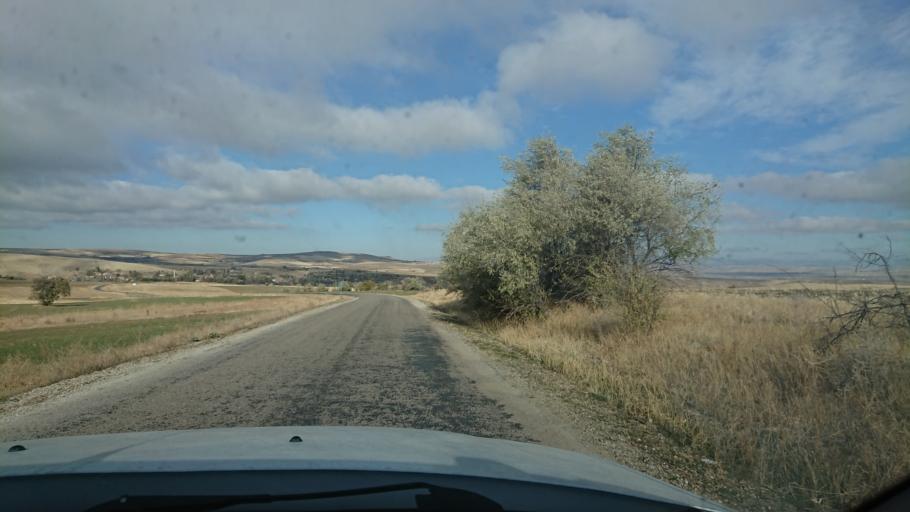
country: TR
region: Aksaray
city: Ortakoy
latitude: 38.7966
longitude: 33.9940
